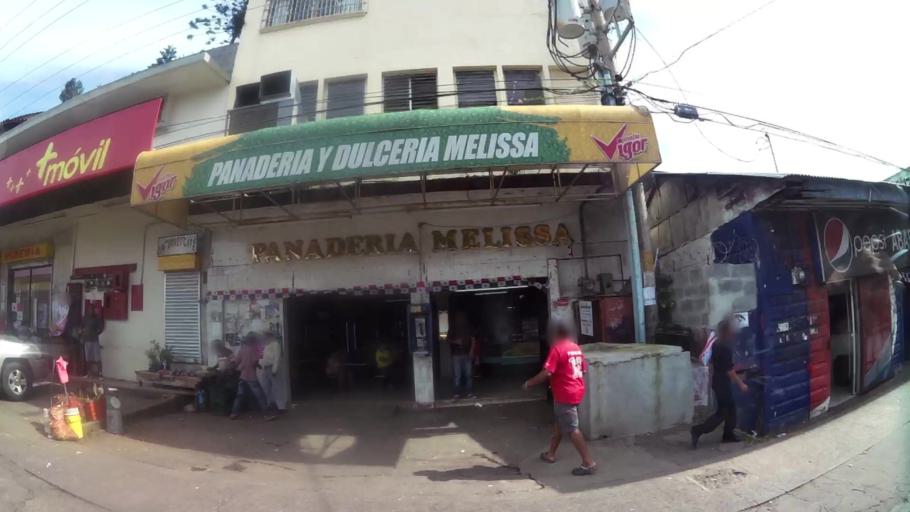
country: PA
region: Panama
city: La Chorrera
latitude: 8.8803
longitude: -79.7806
